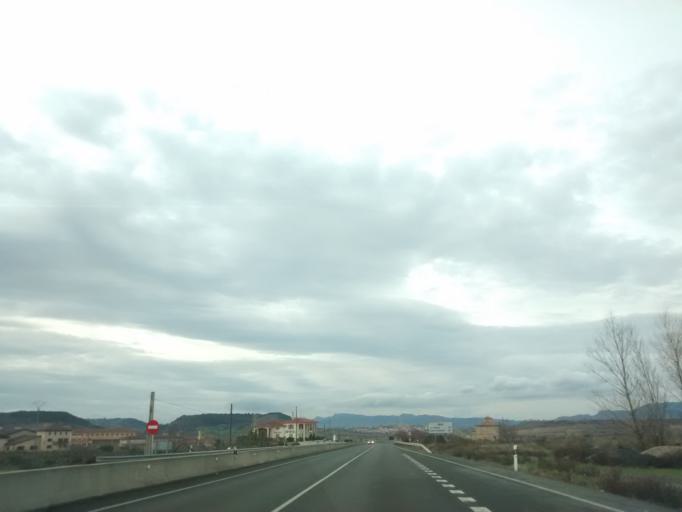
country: ES
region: La Rioja
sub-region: Provincia de La Rioja
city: San Asensio
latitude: 42.5144
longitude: -2.7417
